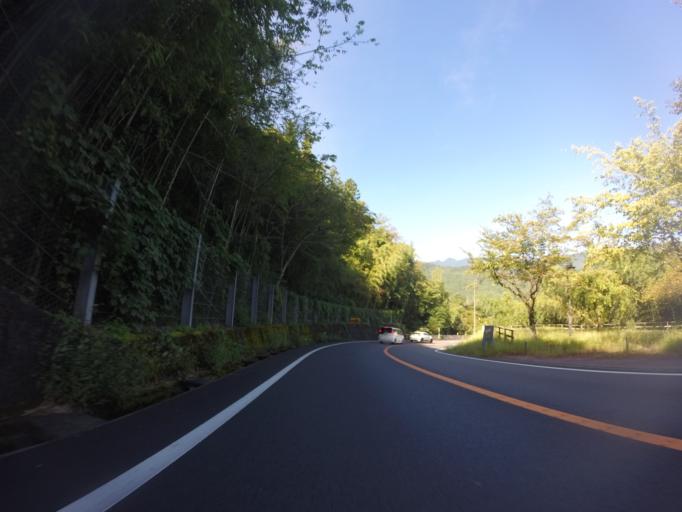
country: JP
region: Shizuoka
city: Fujinomiya
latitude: 35.3539
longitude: 138.4515
